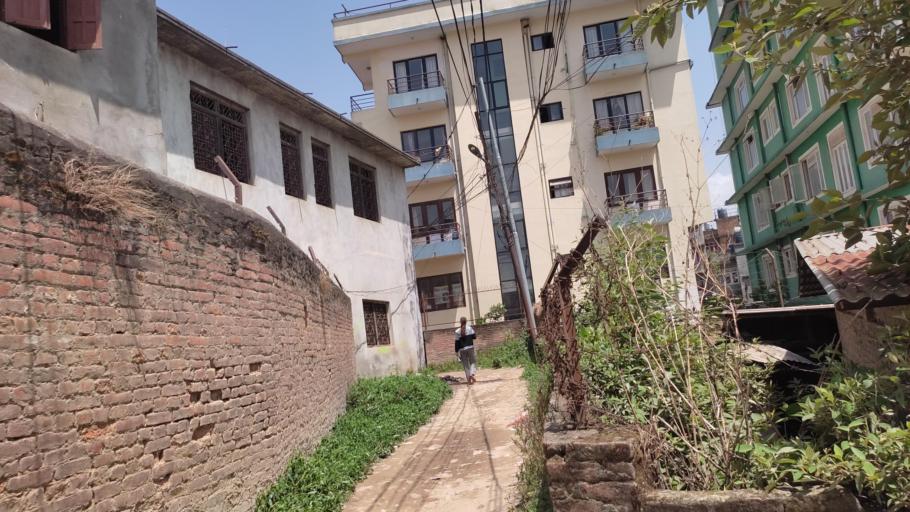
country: NP
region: Central Region
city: Kirtipur
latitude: 27.6753
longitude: 85.2762
